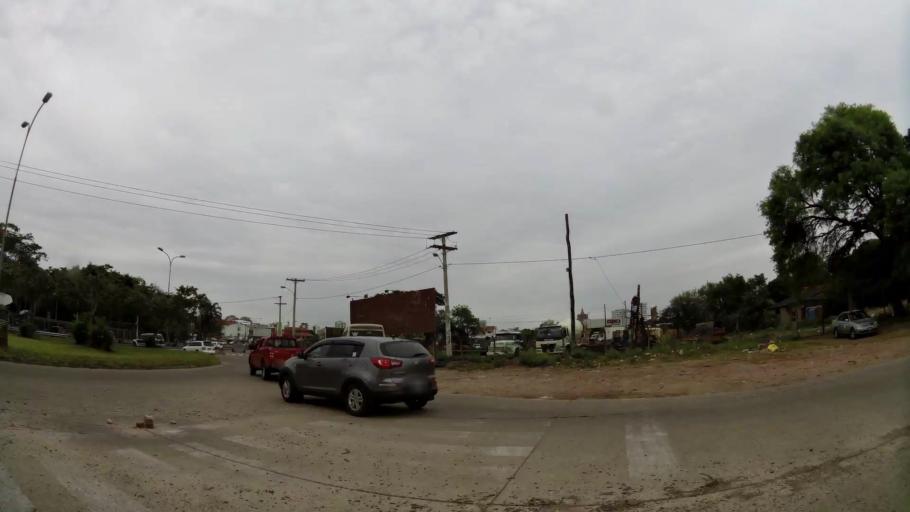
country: BO
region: Santa Cruz
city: Santa Cruz de la Sierra
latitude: -17.7597
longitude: -63.1888
